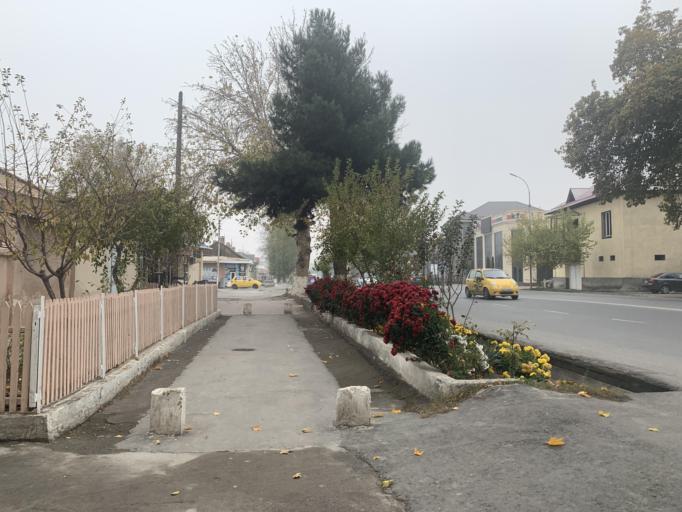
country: UZ
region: Fergana
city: Qo`qon
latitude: 40.5398
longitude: 70.9237
